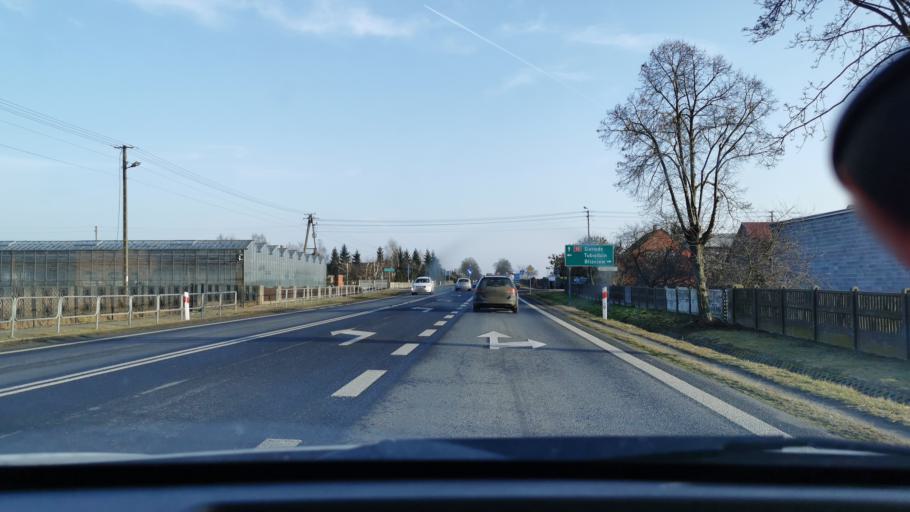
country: PL
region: Lodz Voivodeship
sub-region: Powiat sieradzki
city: Wroblew
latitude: 51.6305
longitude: 18.5502
